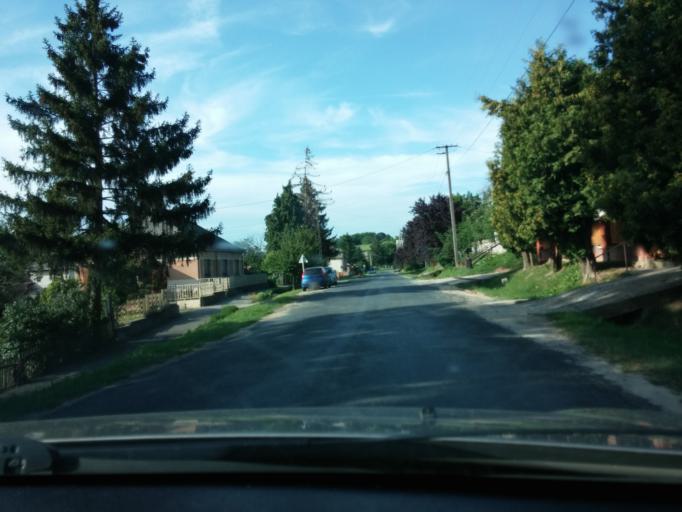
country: HU
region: Somogy
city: Kaposmero
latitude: 46.2729
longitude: 17.7337
